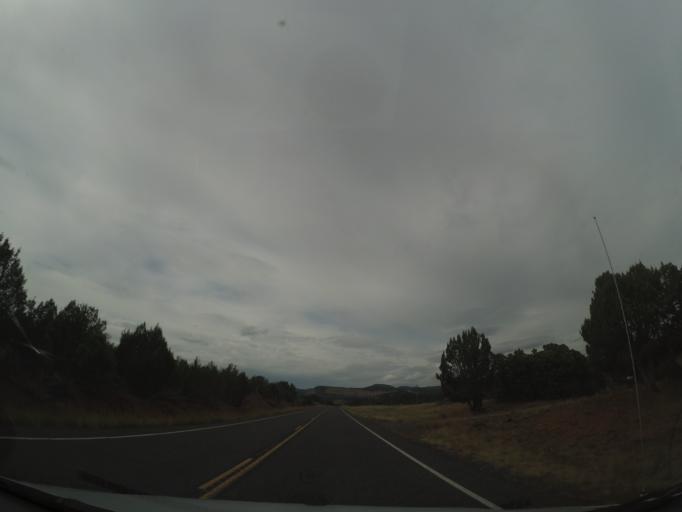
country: US
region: Utah
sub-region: Kane County
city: Kanab
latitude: 37.2509
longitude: -112.7608
